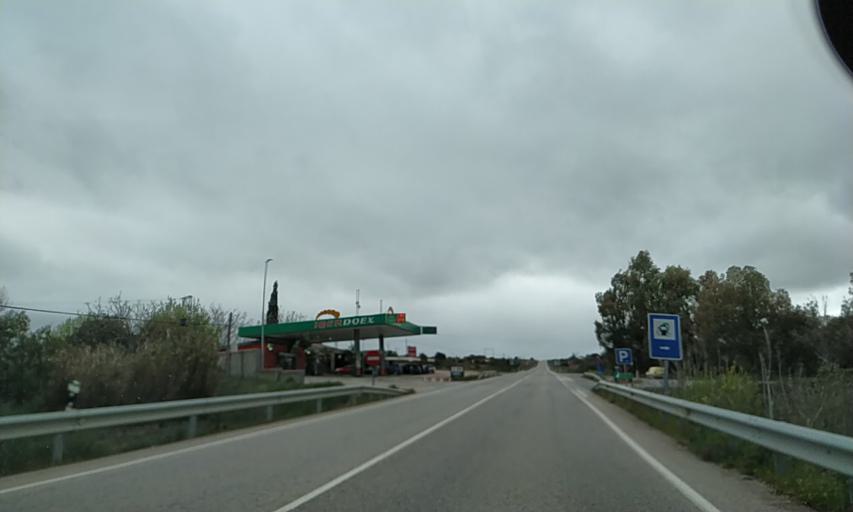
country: ES
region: Extremadura
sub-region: Provincia de Caceres
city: Malpartida de Caceres
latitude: 39.3883
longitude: -6.4351
